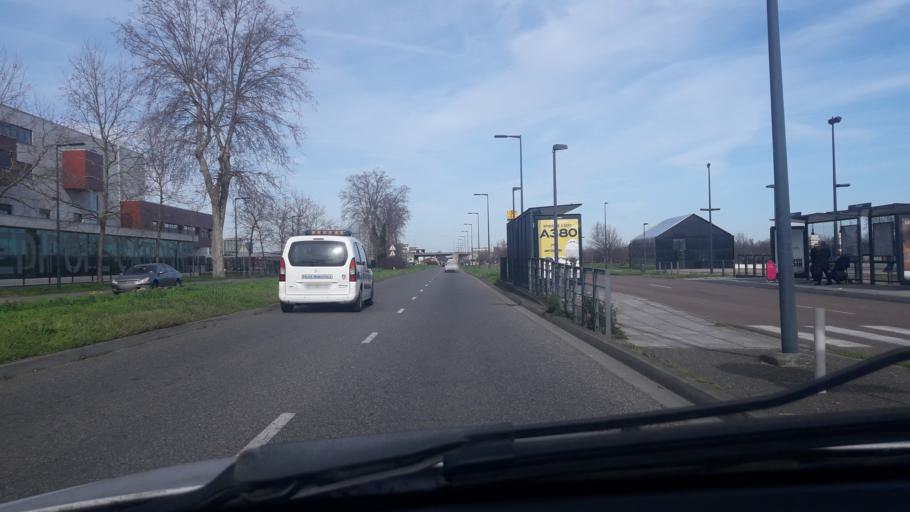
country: FR
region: Midi-Pyrenees
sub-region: Departement de la Haute-Garonne
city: Vieille-Toulouse
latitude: 43.5634
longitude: 1.4252
